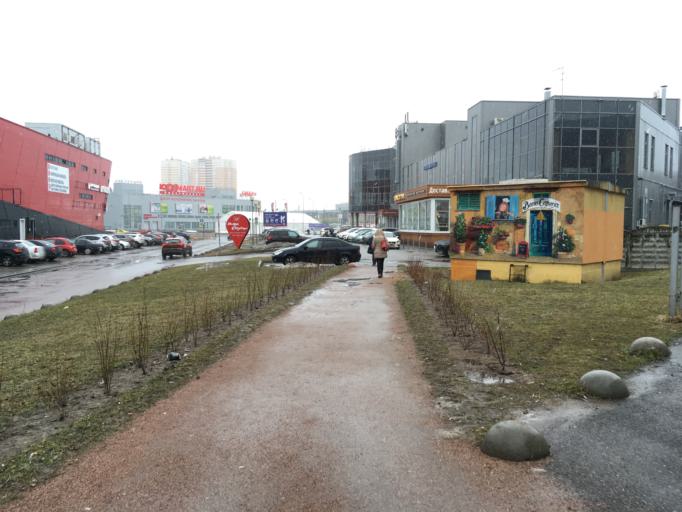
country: RU
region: St.-Petersburg
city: Komendantsky aerodrom
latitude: 60.0018
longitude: 30.2657
